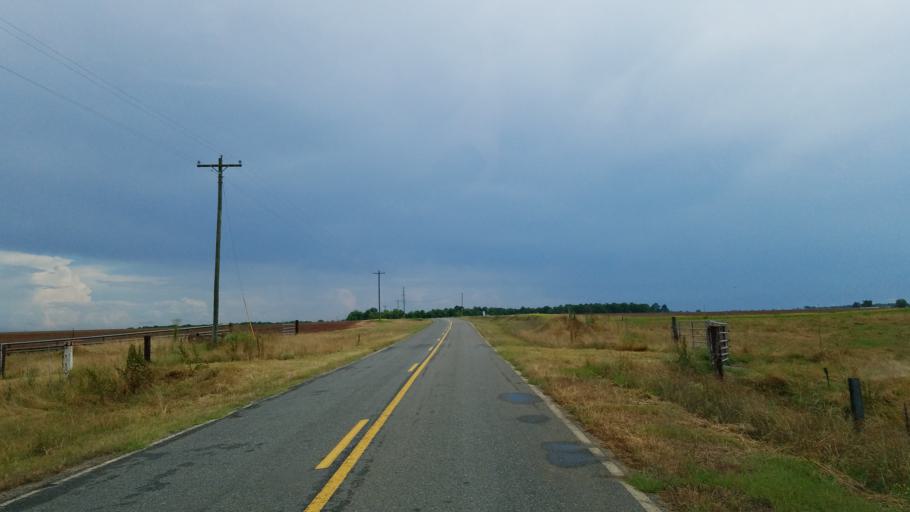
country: US
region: Georgia
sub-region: Dooly County
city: Unadilla
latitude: 32.2827
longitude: -83.7942
